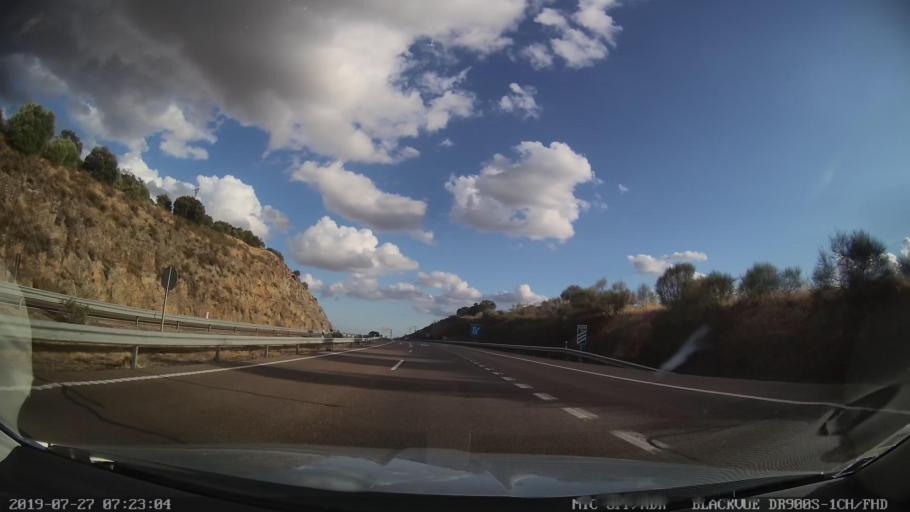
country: ES
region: Extremadura
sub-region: Provincia de Caceres
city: Puerto de Santa Cruz
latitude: 39.3282
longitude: -5.8582
